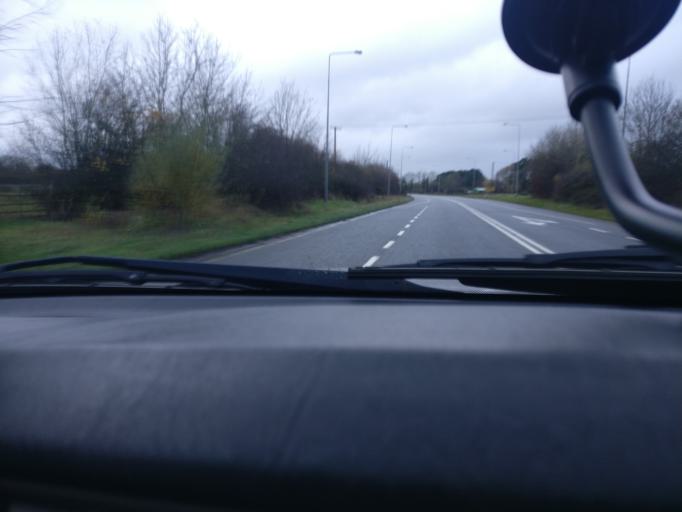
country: IE
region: Leinster
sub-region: Kildare
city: Kilcock
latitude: 53.4087
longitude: -6.7019
